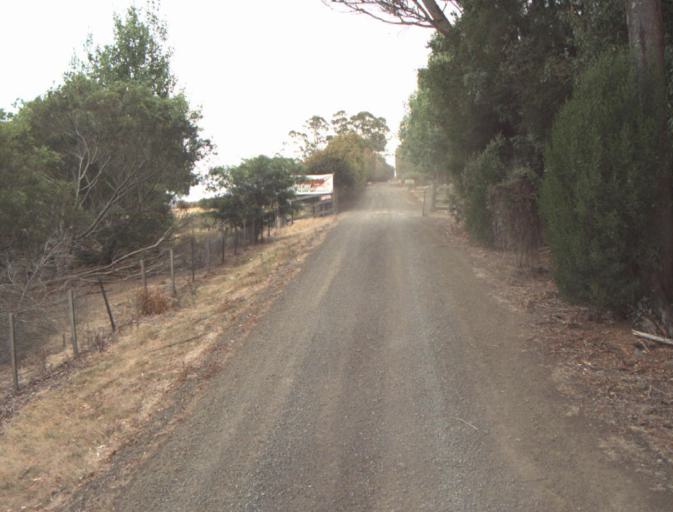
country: AU
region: Tasmania
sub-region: Launceston
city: Mayfield
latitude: -41.2717
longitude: 147.1850
